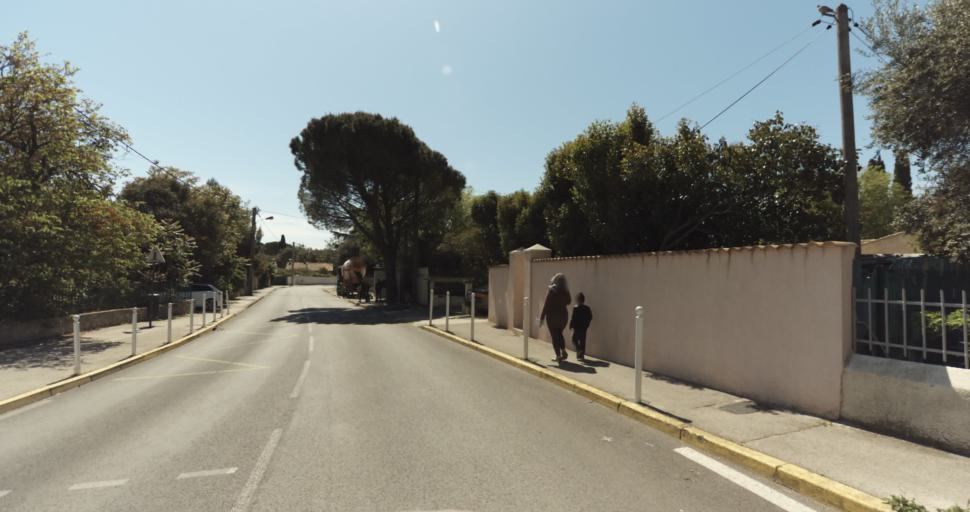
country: FR
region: Provence-Alpes-Cote d'Azur
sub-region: Departement du Var
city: Toulon
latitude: 43.1416
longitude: 5.9022
